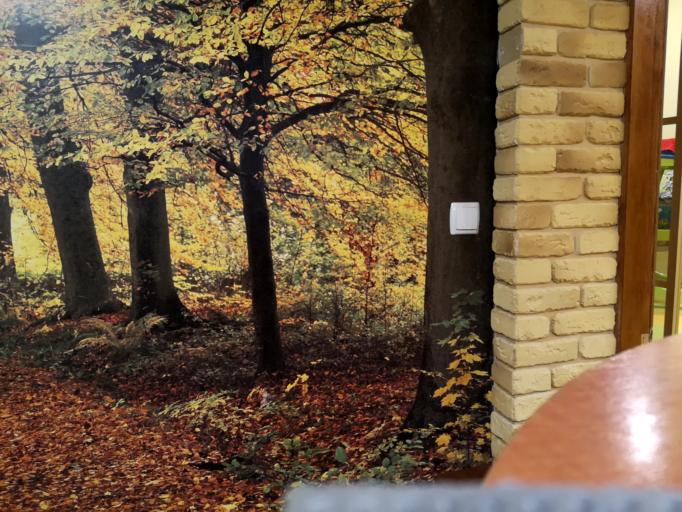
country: RU
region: Sverdlovsk
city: Krasnotur'insk
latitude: 59.9071
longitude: 60.2621
